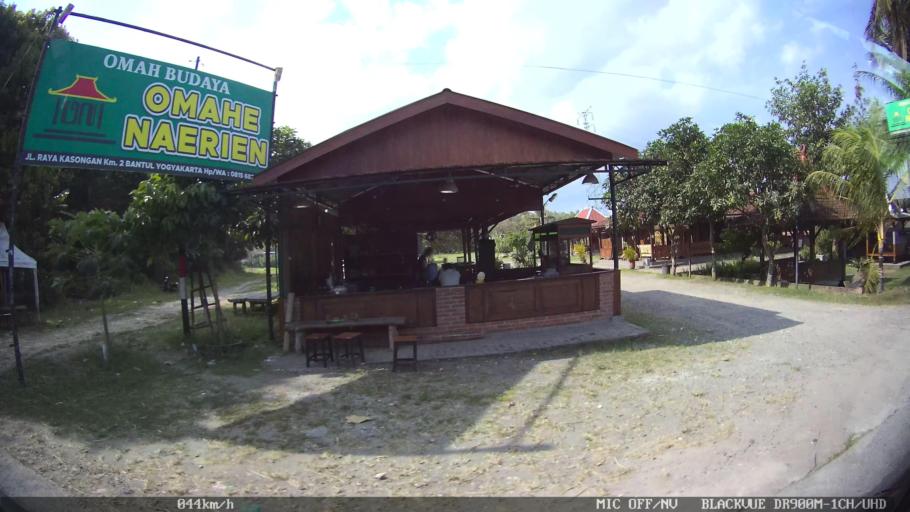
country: ID
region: Daerah Istimewa Yogyakarta
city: Kasihan
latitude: -7.8408
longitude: 110.3264
